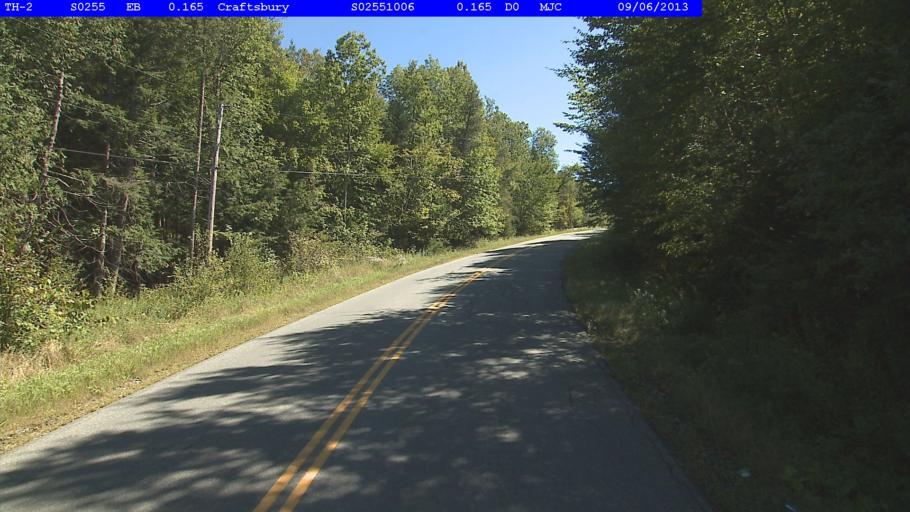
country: US
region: Vermont
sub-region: Caledonia County
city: Hardwick
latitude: 44.6284
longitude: -72.3608
